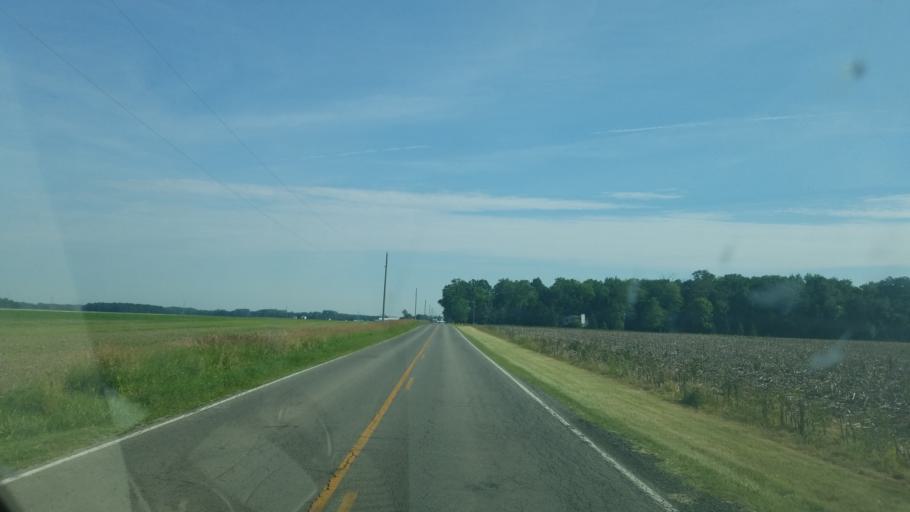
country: US
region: Ohio
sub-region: Hancock County
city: Findlay
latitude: 41.0106
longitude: -83.5881
